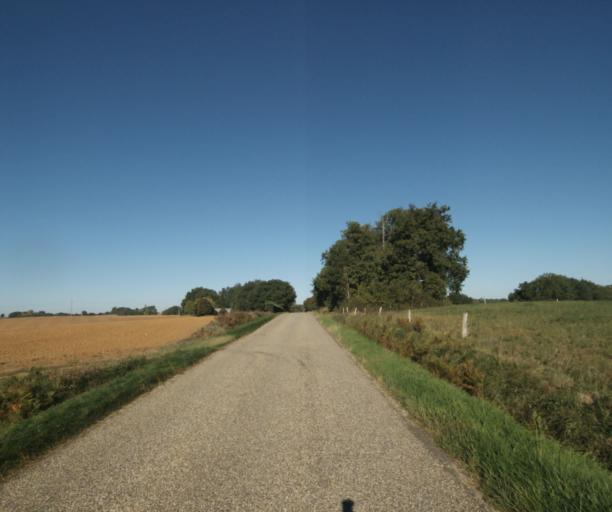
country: FR
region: Midi-Pyrenees
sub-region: Departement du Gers
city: Vic-Fezensac
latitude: 43.8242
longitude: 0.2717
